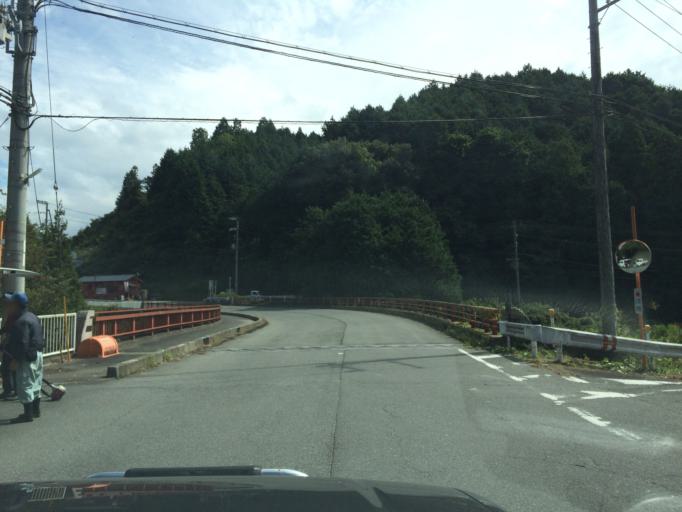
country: JP
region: Mie
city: Nabari
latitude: 34.6813
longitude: 136.0341
